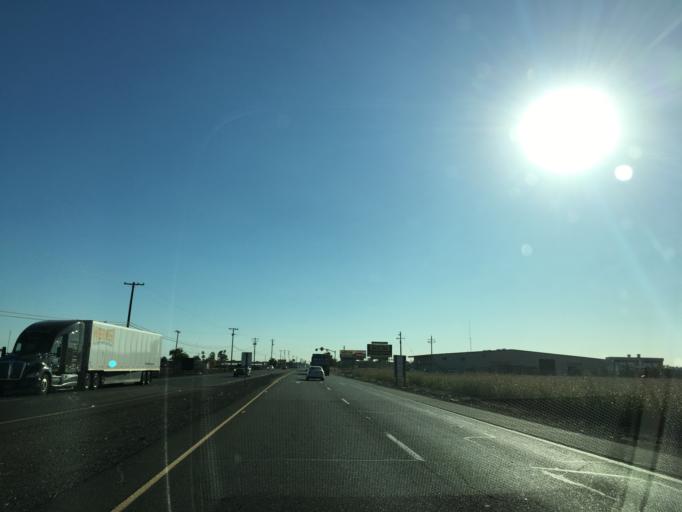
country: US
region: California
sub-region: Merced County
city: Los Banos
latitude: 37.0568
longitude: -120.8875
